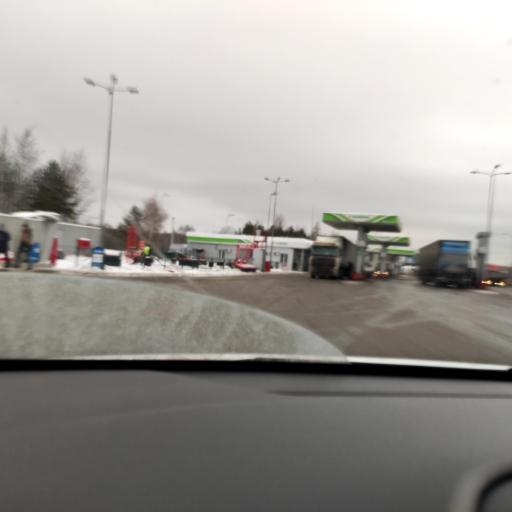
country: RU
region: Tatarstan
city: Osinovo
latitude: 55.8945
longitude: 48.8813
